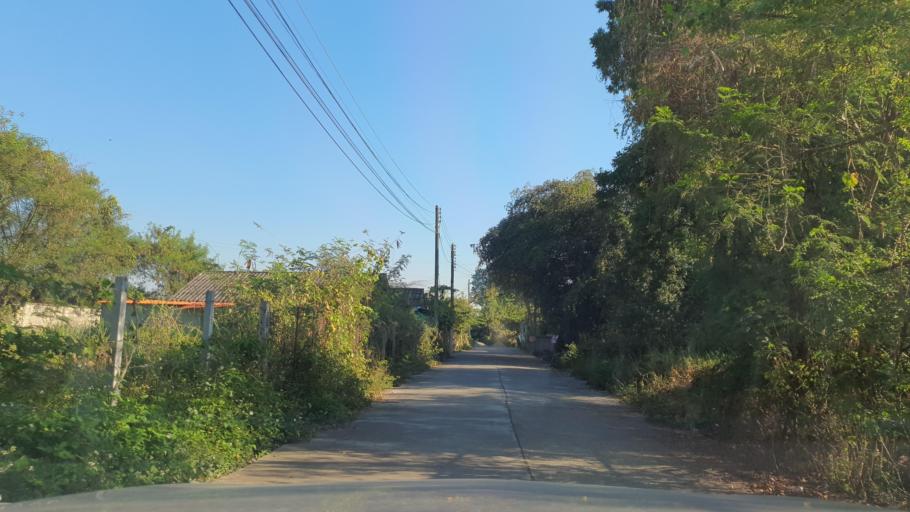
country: TH
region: Chiang Mai
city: Hang Dong
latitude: 18.6950
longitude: 98.9470
